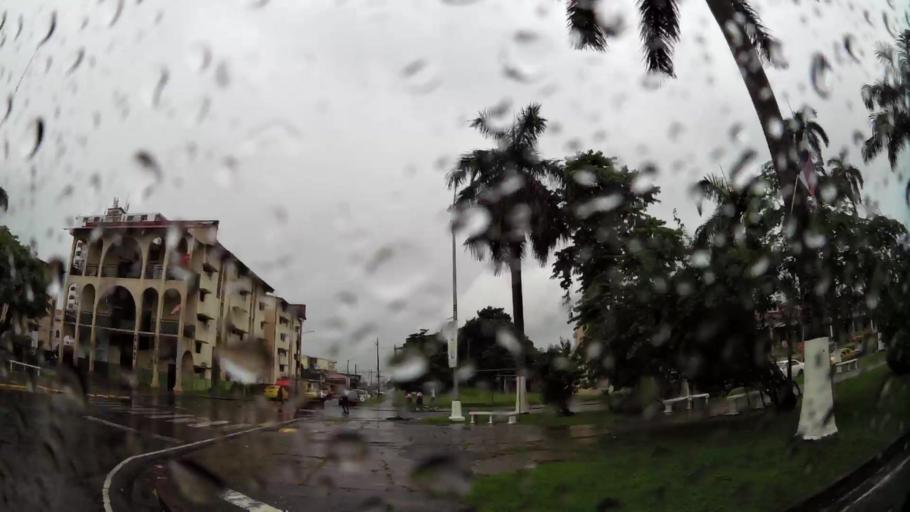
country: PA
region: Colon
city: Colon
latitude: 9.3627
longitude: -79.9030
